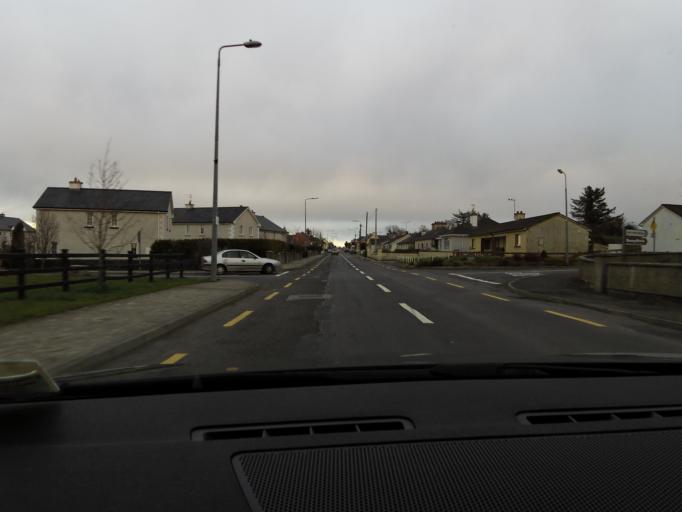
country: IE
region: Connaught
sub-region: Sligo
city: Ballymote
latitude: 53.9972
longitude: -8.5255
